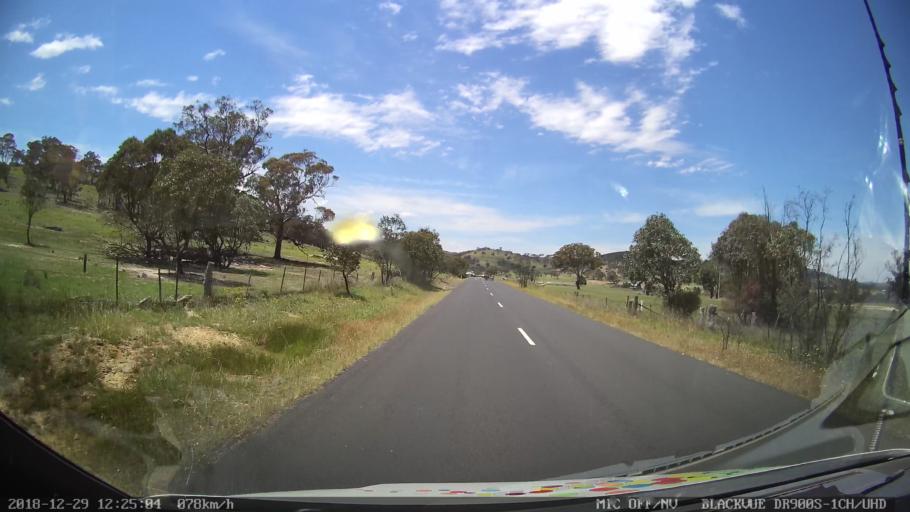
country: AU
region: Australian Capital Territory
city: Macarthur
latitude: -35.4527
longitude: 149.2113
